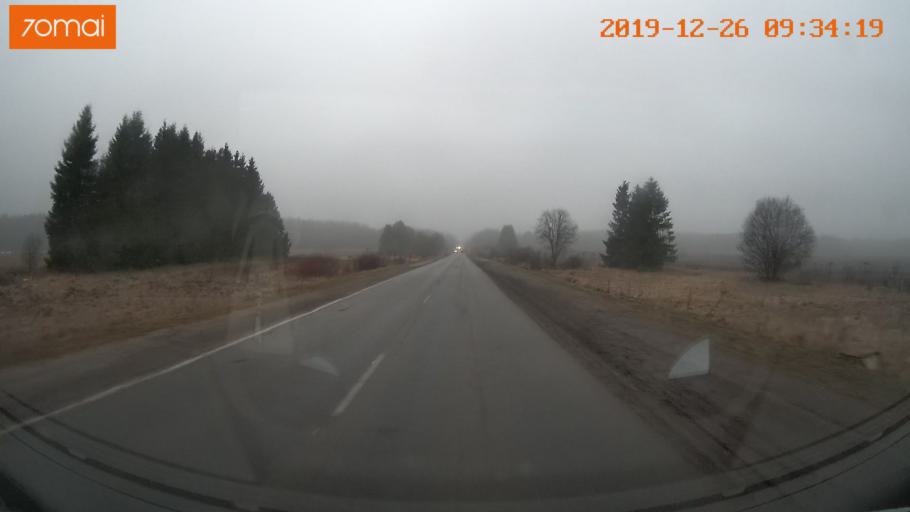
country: RU
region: Vologda
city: Vologda
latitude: 59.1000
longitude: 40.0880
